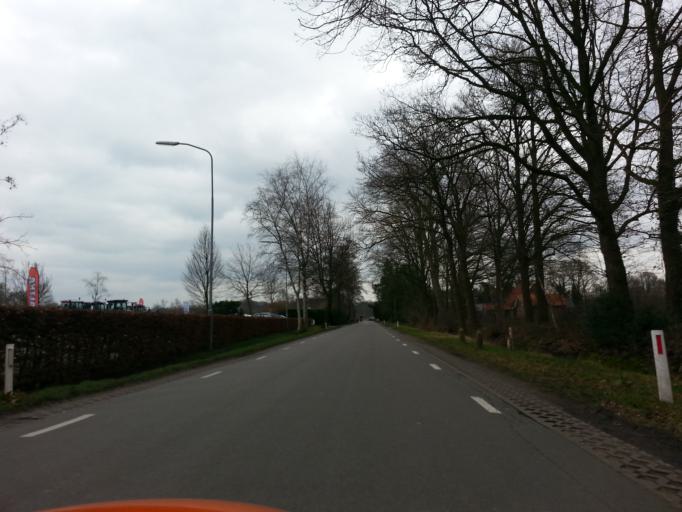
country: NL
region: Utrecht
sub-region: Gemeente Leusden
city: Leusden
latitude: 52.1245
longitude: 5.4817
